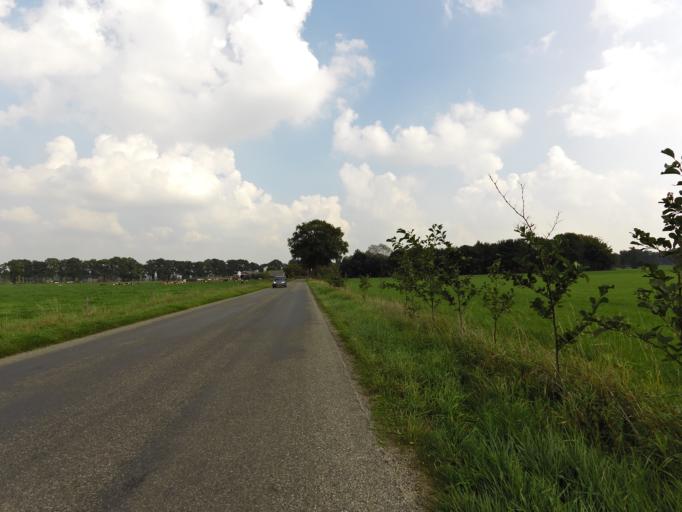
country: NL
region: Gelderland
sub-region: Oude IJsselstreek
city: Wisch
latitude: 51.9111
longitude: 6.4243
